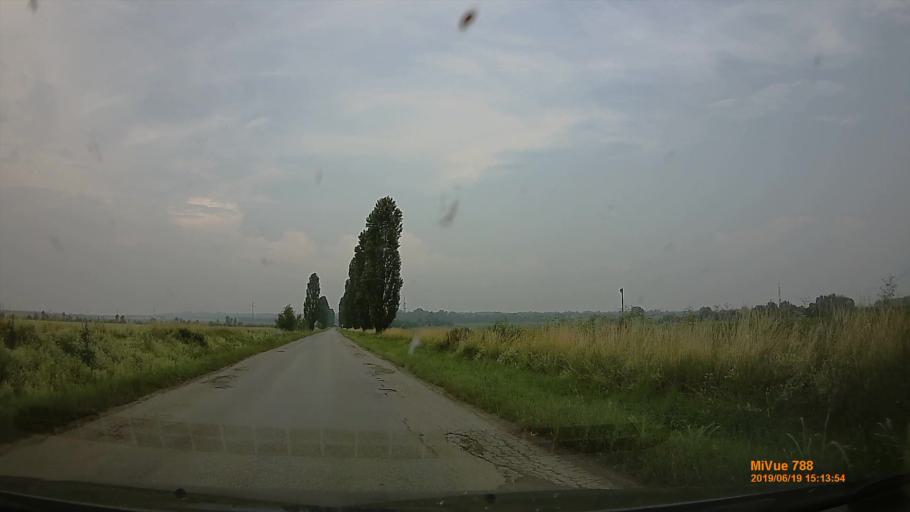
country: HU
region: Baranya
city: Szigetvar
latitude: 46.0642
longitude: 17.8197
